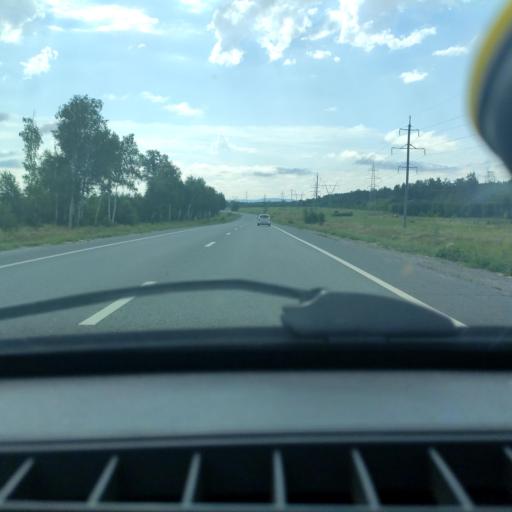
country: RU
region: Samara
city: Bogatyr'
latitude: 53.4948
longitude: 49.9652
